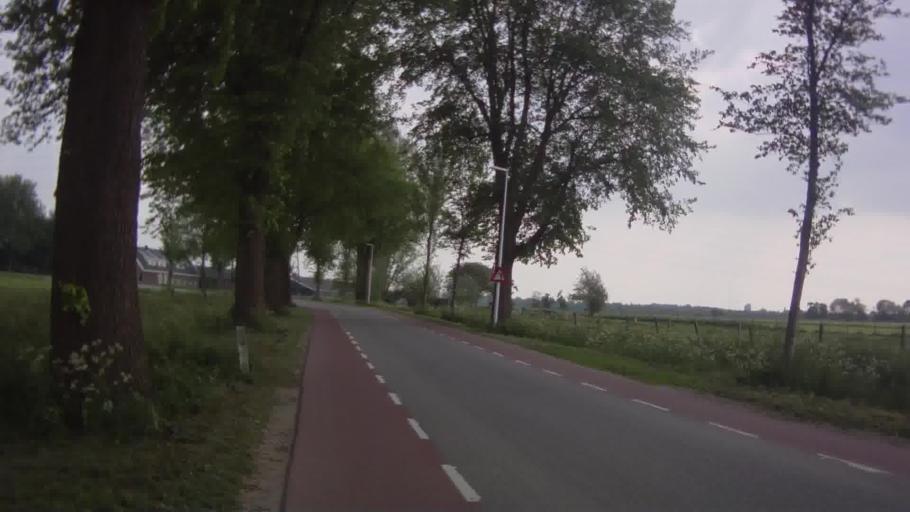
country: NL
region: Utrecht
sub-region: Gemeente Bunnik
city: Bunnik
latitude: 52.0539
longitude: 5.1875
